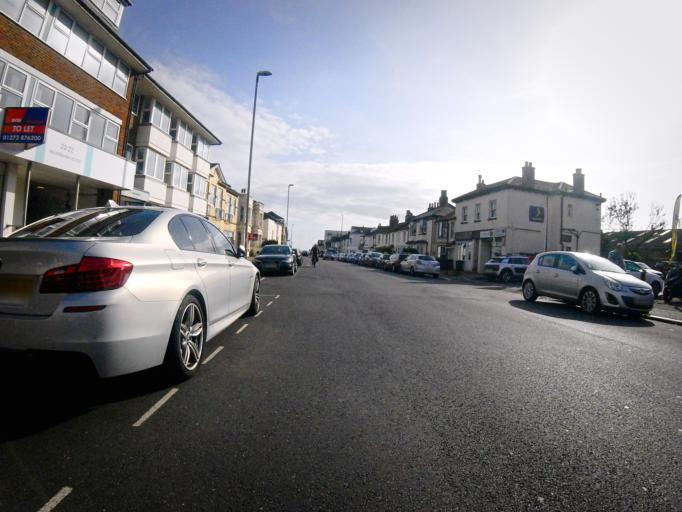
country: GB
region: England
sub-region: East Sussex
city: Portslade
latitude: 50.8311
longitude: -0.2082
